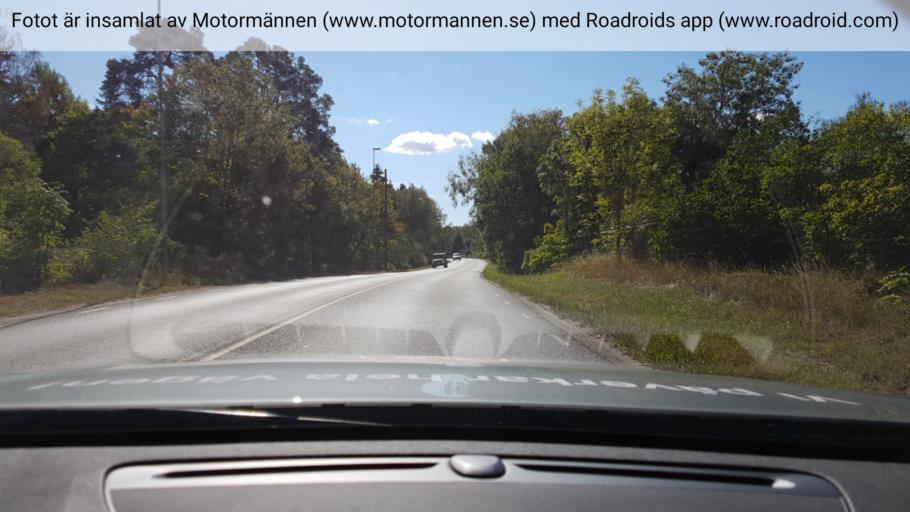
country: SE
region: Stockholm
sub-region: Nacka Kommun
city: Fisksatra
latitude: 59.2443
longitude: 18.2762
